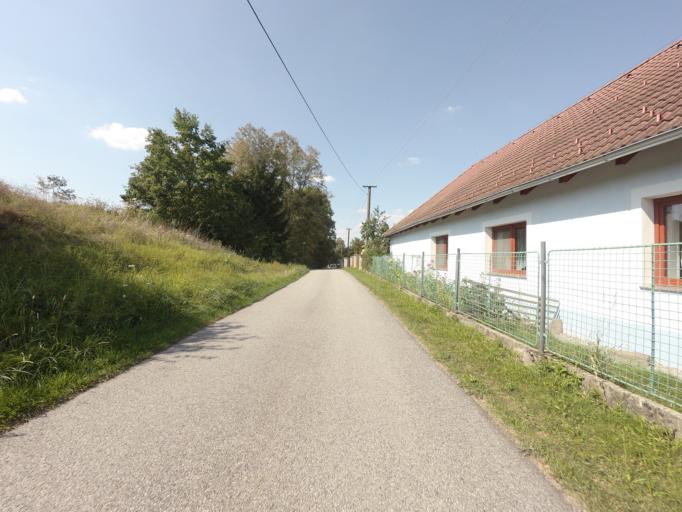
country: CZ
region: Jihocesky
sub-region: Okres Ceske Budejovice
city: Hluboka nad Vltavou
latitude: 49.1239
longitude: 14.4555
